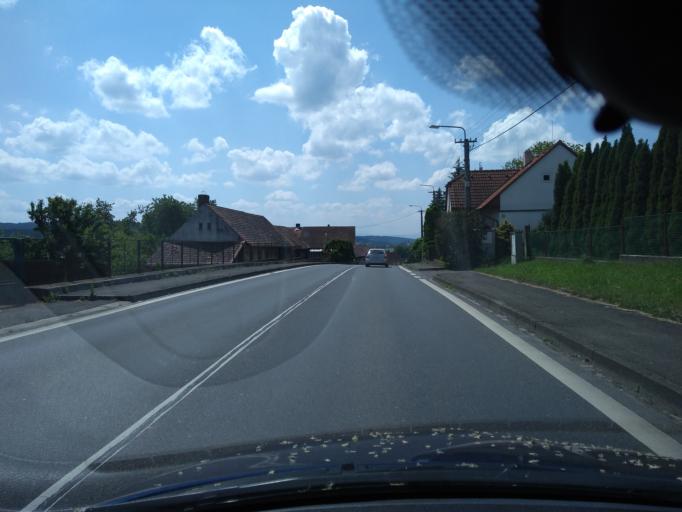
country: CZ
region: Plzensky
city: Svihov
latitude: 49.5032
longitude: 13.2948
